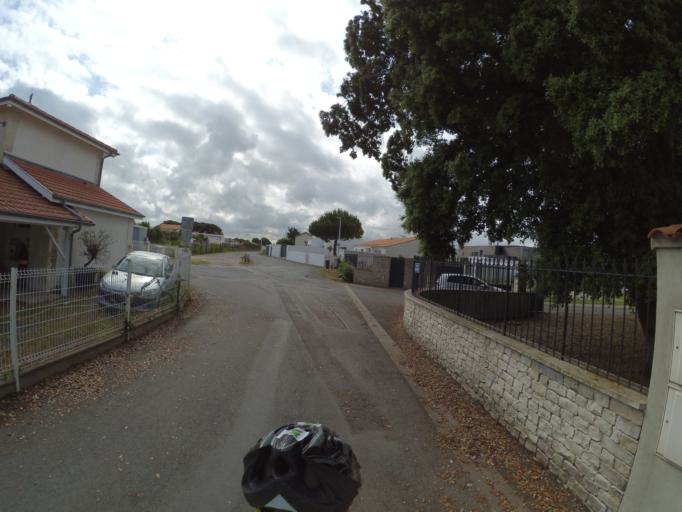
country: FR
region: Poitou-Charentes
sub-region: Departement de la Charente-Maritime
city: Angoulins
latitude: 46.0993
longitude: -1.1085
